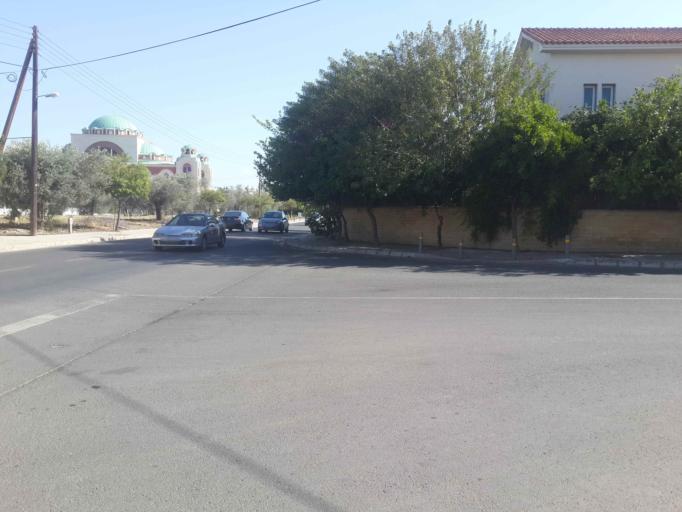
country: CY
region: Lefkosia
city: Nicosia
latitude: 35.1495
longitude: 33.3346
